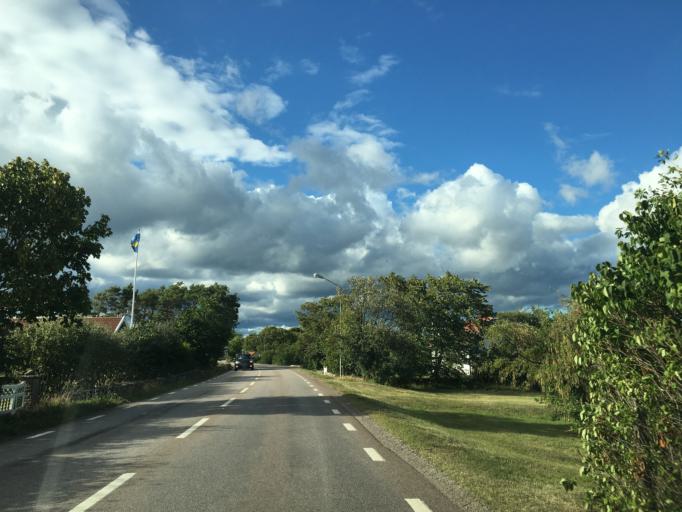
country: SE
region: Kalmar
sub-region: Morbylanga Kommun
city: Moerbylanga
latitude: 56.5388
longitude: 16.4460
